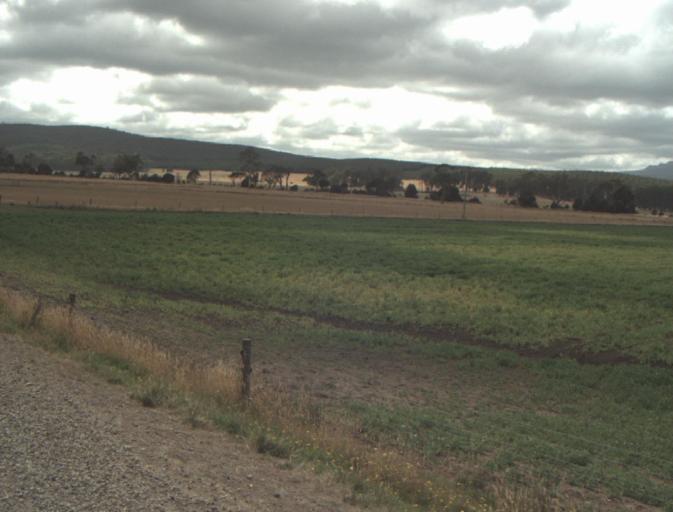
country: AU
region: Tasmania
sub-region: Northern Midlands
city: Evandale
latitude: -41.4800
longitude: 147.4432
